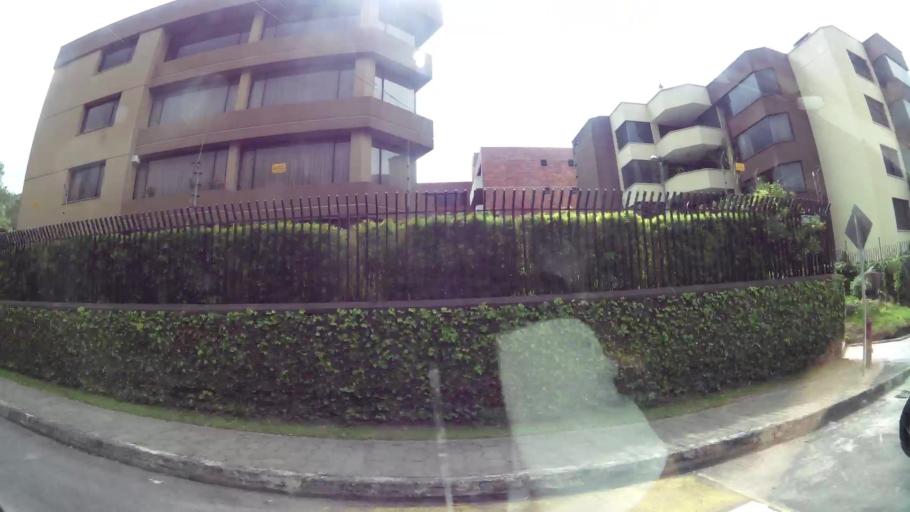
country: EC
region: Pichincha
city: Quito
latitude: -0.1688
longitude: -78.4944
